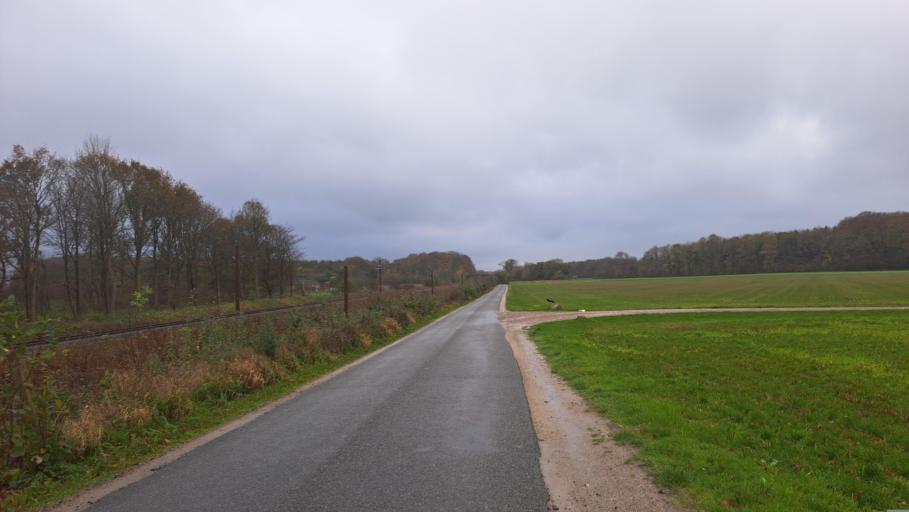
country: DK
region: Central Jutland
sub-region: Hedensted Kommune
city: Hedensted
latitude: 55.8251
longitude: 9.7277
